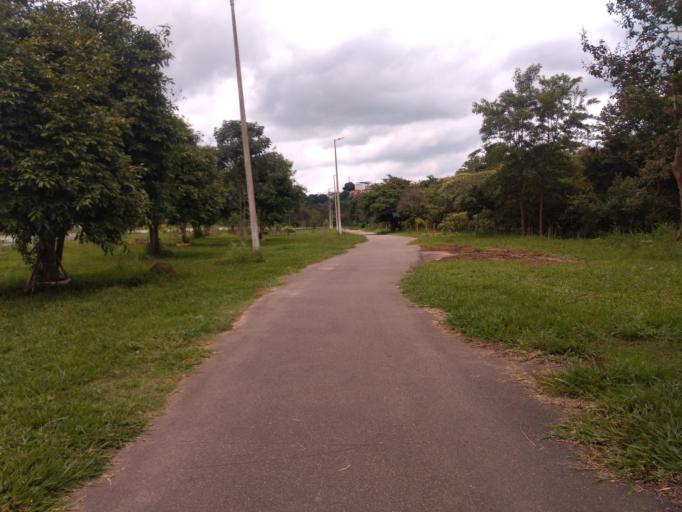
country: BR
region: Minas Gerais
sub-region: Tres Coracoes
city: Tres Coracoes
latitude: -21.7010
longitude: -45.2442
